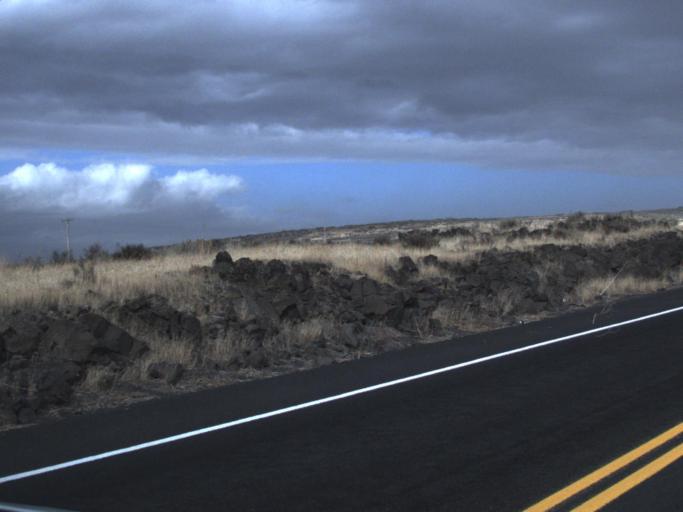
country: US
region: Washington
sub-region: Adams County
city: Ritzville
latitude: 47.3352
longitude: -118.6557
